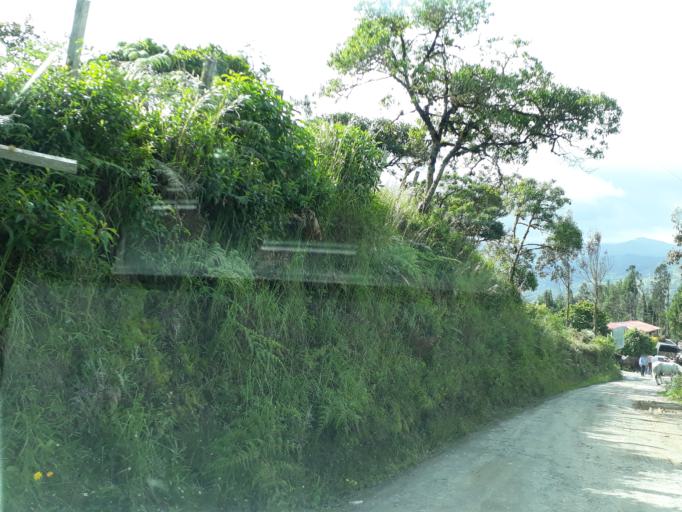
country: CO
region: Cundinamarca
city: Junin
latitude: 4.7728
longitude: -73.6203
